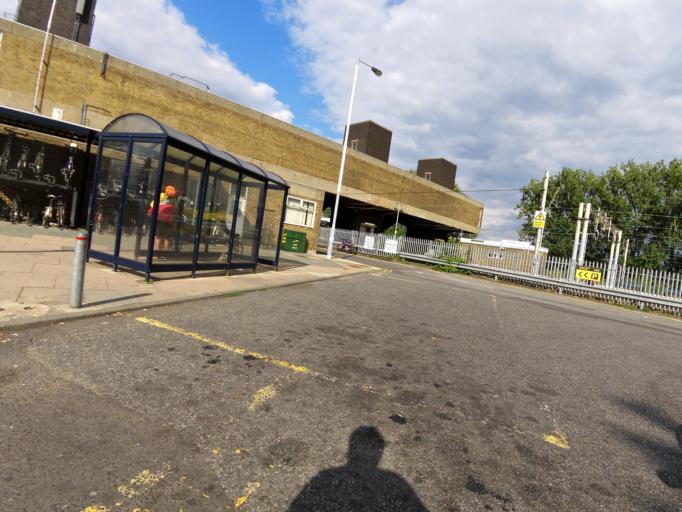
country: GB
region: England
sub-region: Hertfordshire
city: Broxbourne
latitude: 51.7467
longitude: -0.0113
